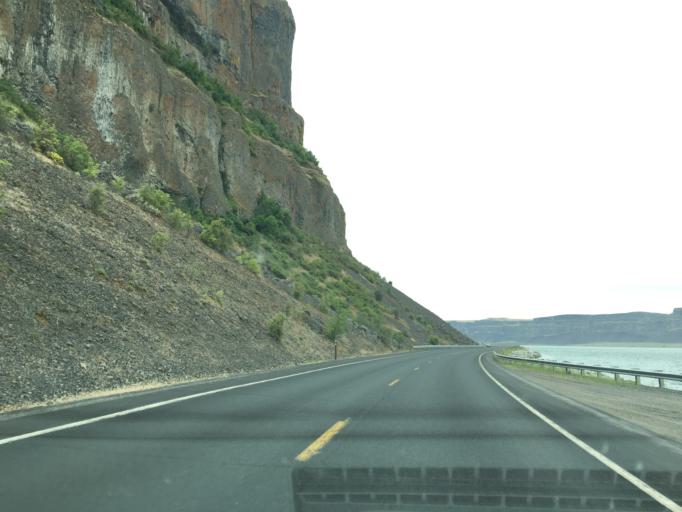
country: US
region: Washington
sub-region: Okanogan County
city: Coulee Dam
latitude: 47.8156
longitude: -119.1550
